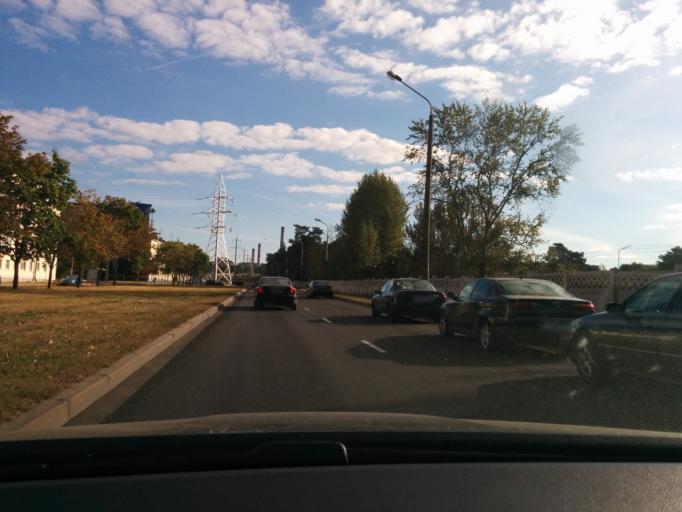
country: BY
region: Minsk
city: Minsk
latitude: 53.8656
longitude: 27.6317
